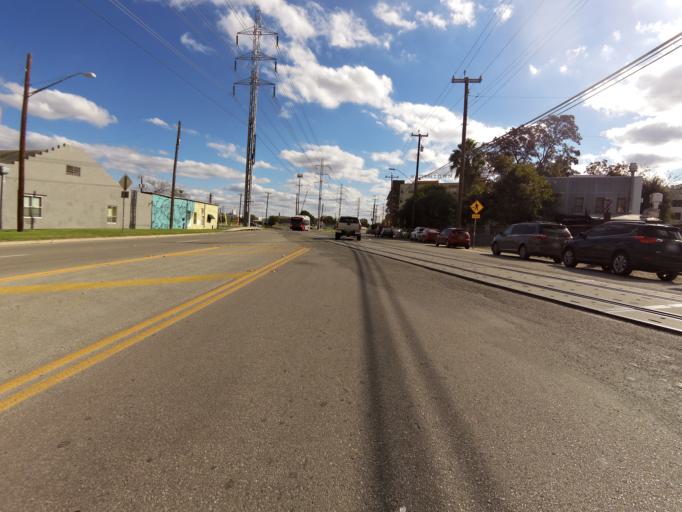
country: US
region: Texas
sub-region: Bexar County
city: San Antonio
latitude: 29.4084
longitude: -98.4961
